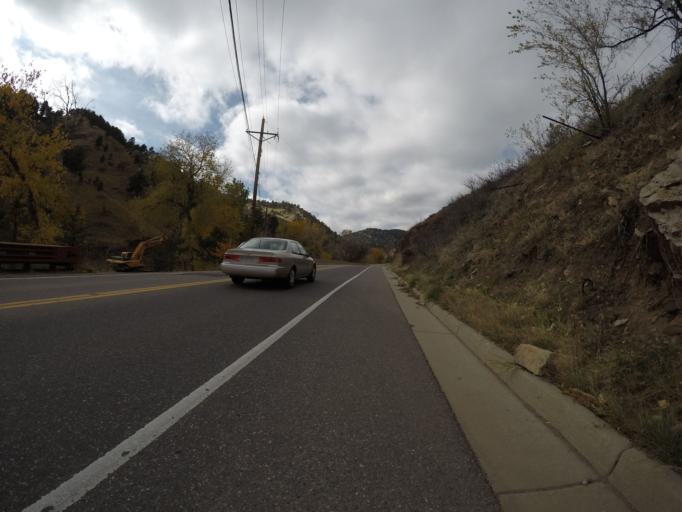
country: US
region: Colorado
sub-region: Boulder County
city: Boulder
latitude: 40.0635
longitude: -105.2964
